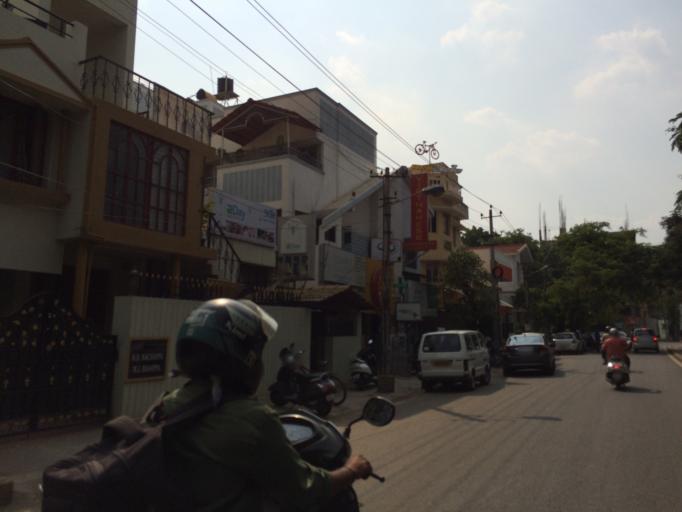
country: IN
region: Karnataka
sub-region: Bangalore Urban
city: Bangalore
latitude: 12.9662
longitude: 77.6375
